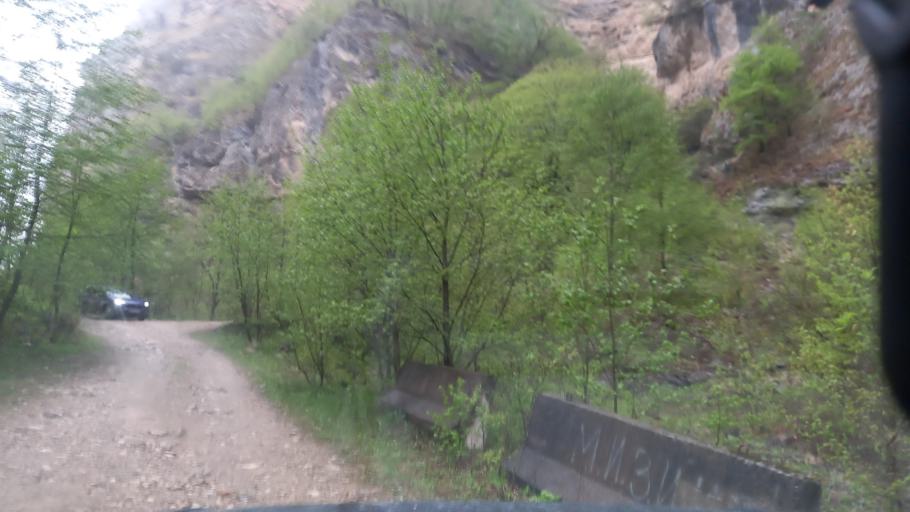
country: RU
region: Kabardino-Balkariya
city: Bylym
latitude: 43.5917
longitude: 42.9950
